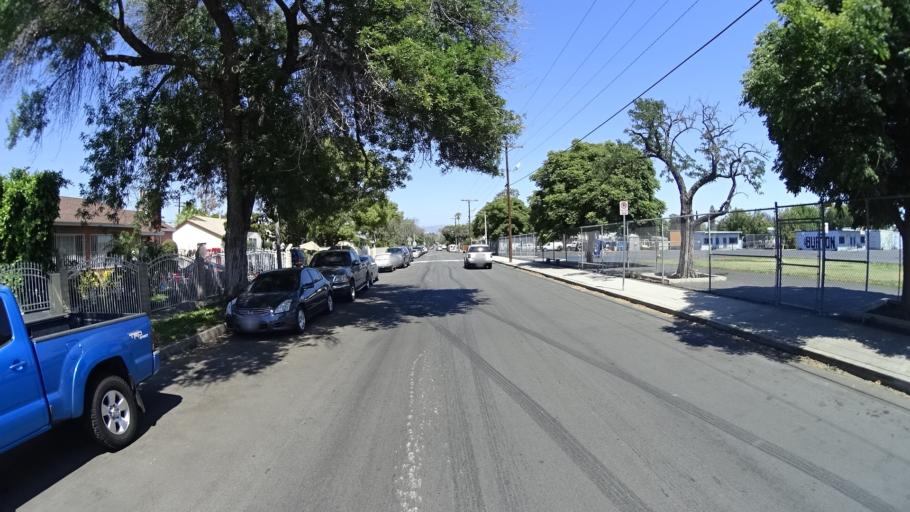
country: US
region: California
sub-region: Los Angeles County
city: Van Nuys
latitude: 34.2207
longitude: -118.4418
